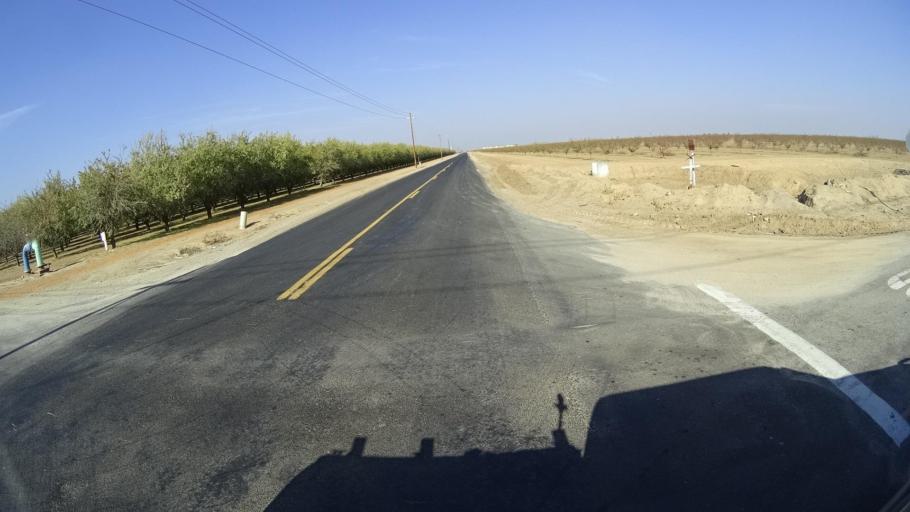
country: US
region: California
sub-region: Kern County
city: Shafter
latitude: 35.5297
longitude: -119.1515
